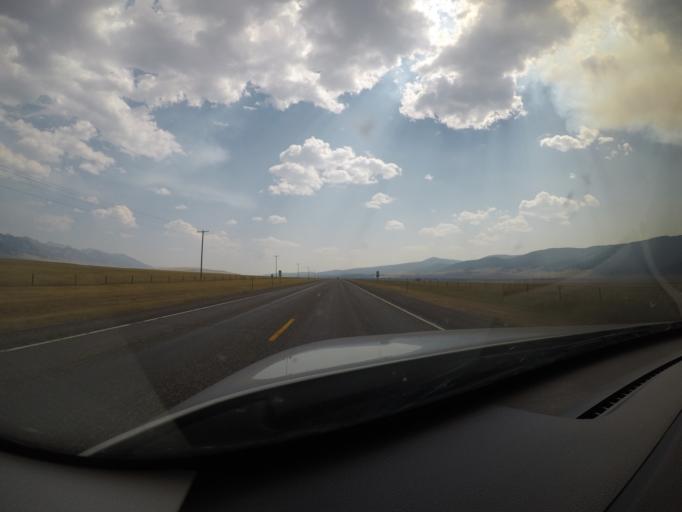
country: US
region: Montana
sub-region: Gallatin County
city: Big Sky
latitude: 45.0198
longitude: -111.6483
